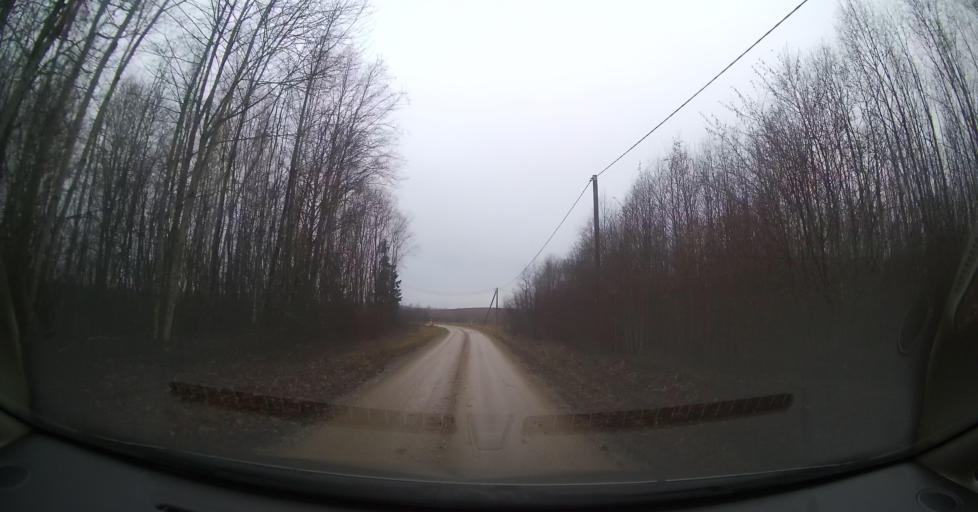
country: EE
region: Tartu
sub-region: Tartu linn
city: Tartu
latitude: 58.3900
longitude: 27.0012
